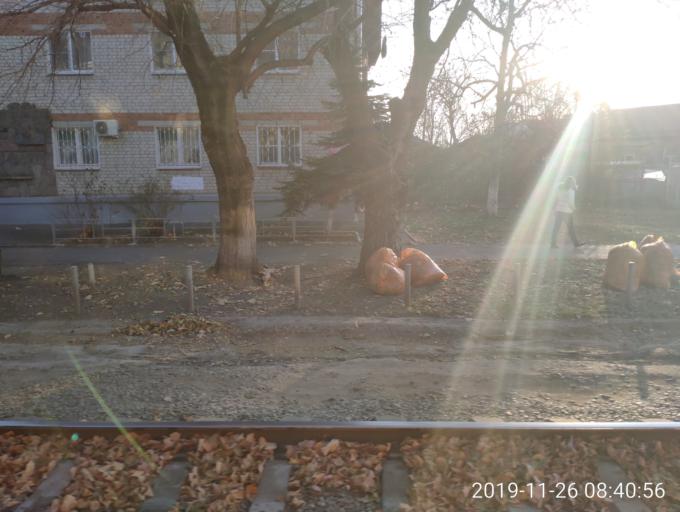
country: RU
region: Krasnodarskiy
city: Krasnodar
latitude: 45.0545
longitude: 38.9838
